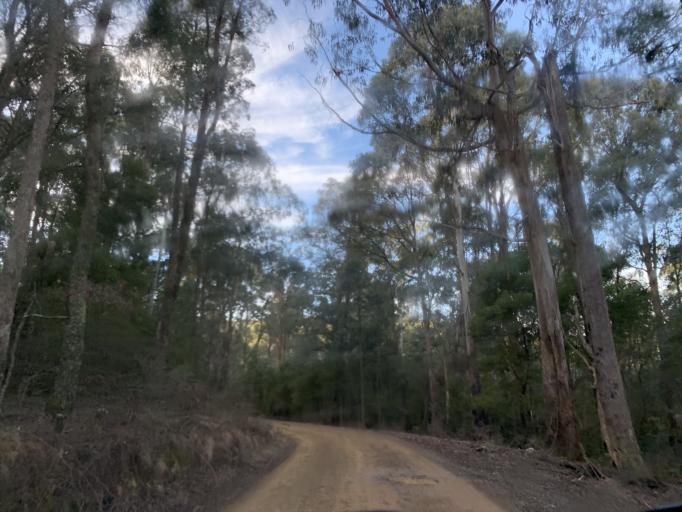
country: AU
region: Victoria
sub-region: Mansfield
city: Mansfield
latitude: -36.8902
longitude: 146.1201
